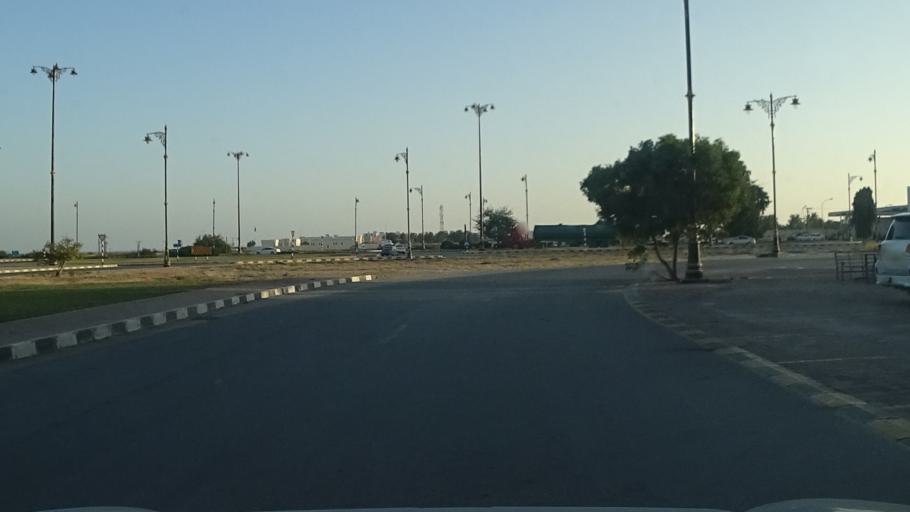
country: OM
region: Zufar
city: Salalah
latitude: 17.0271
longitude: 54.1722
